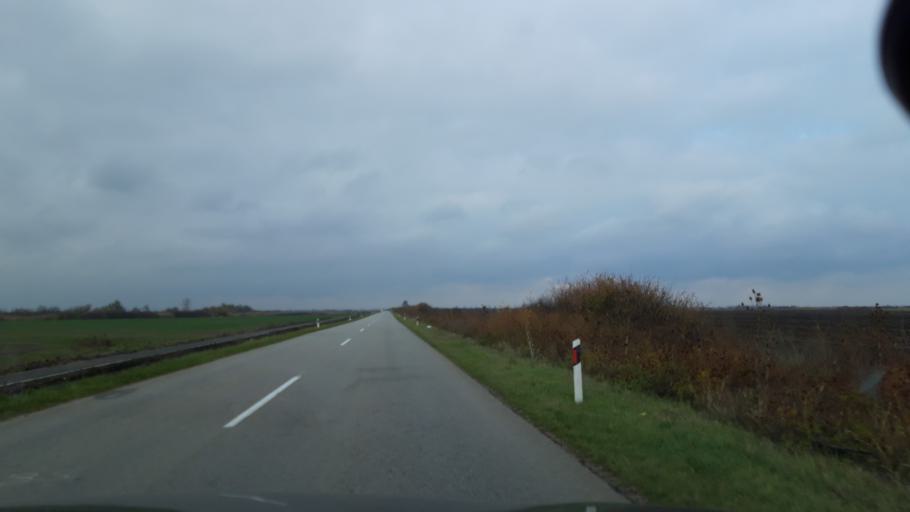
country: RS
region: Autonomna Pokrajina Vojvodina
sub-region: Severnobanatski Okrug
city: Novi Knezevac
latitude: 46.0836
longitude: 20.1066
